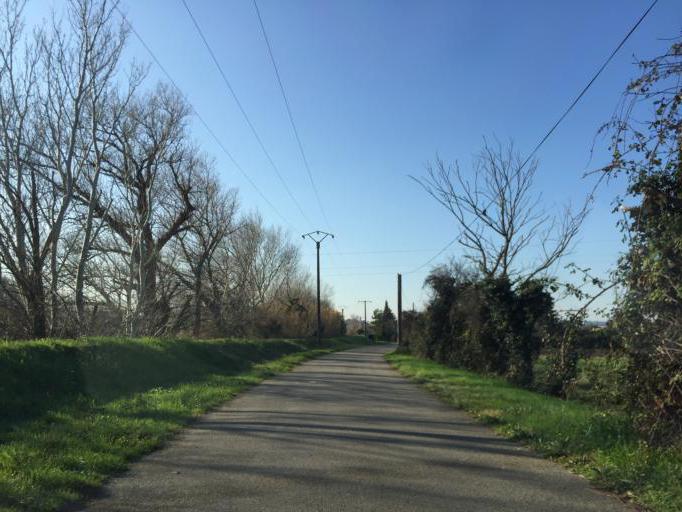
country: FR
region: Provence-Alpes-Cote d'Azur
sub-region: Departement du Vaucluse
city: Bedarrides
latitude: 44.0396
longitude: 4.9100
